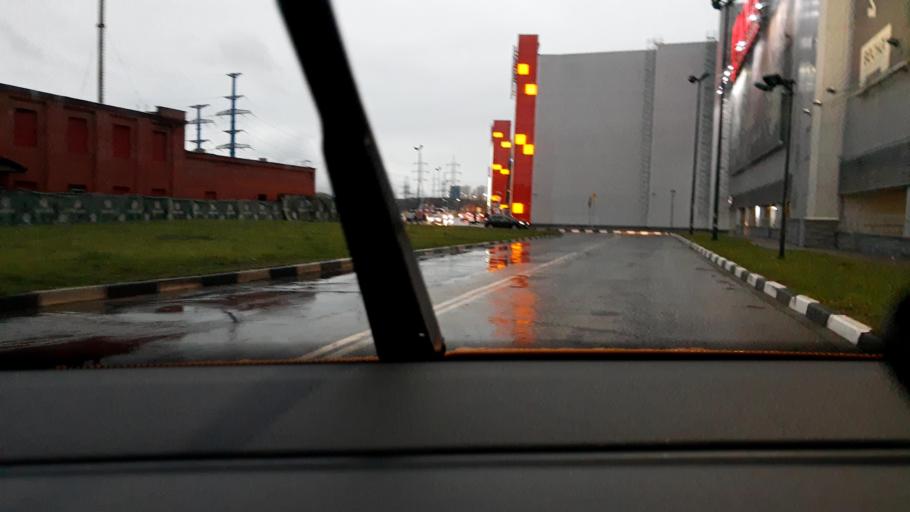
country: RU
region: Moscow
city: Lianozovo
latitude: 55.9124
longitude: 37.5881
